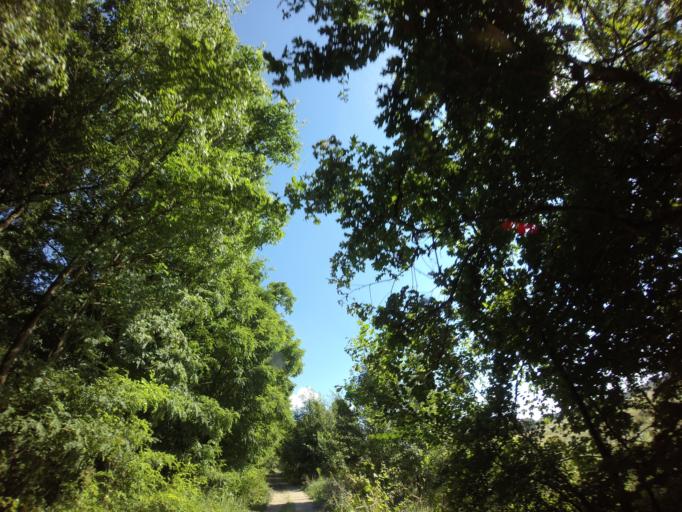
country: PL
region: West Pomeranian Voivodeship
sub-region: Powiat choszczenski
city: Recz
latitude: 53.2229
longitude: 15.6284
